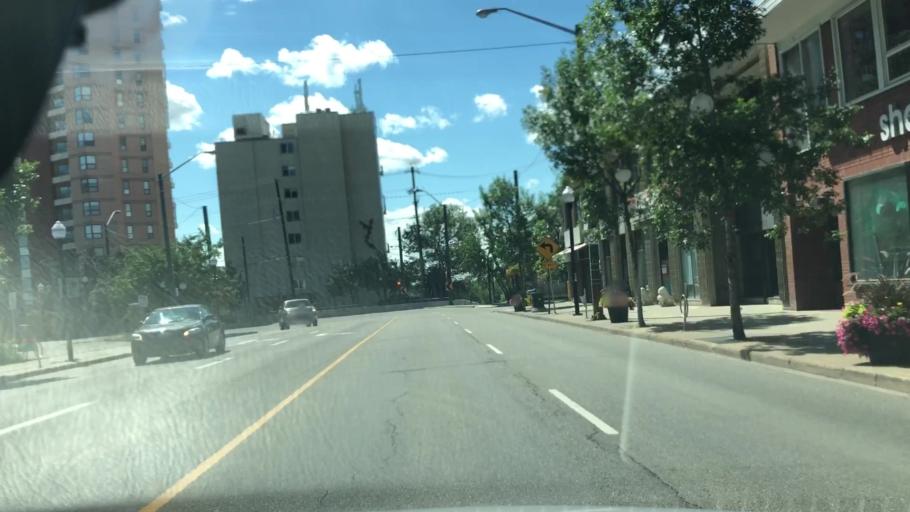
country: CA
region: Alberta
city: Edmonton
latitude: 53.5421
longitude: -113.5359
